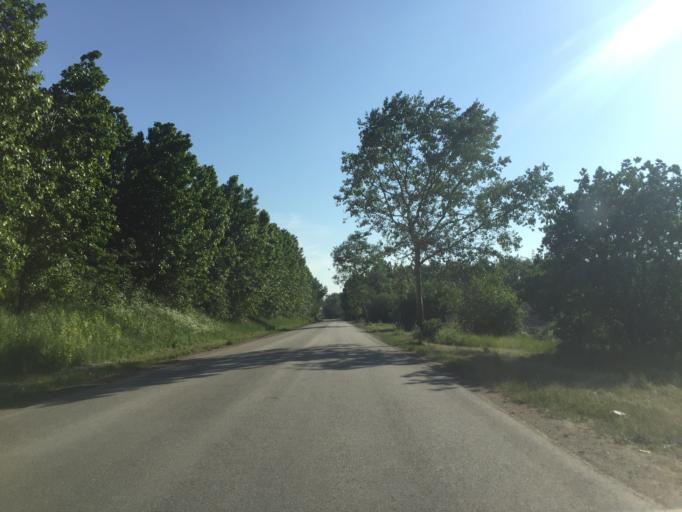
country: DK
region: Capital Region
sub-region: Frederiksberg Kommune
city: Frederiksberg
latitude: 55.6313
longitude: 12.5403
